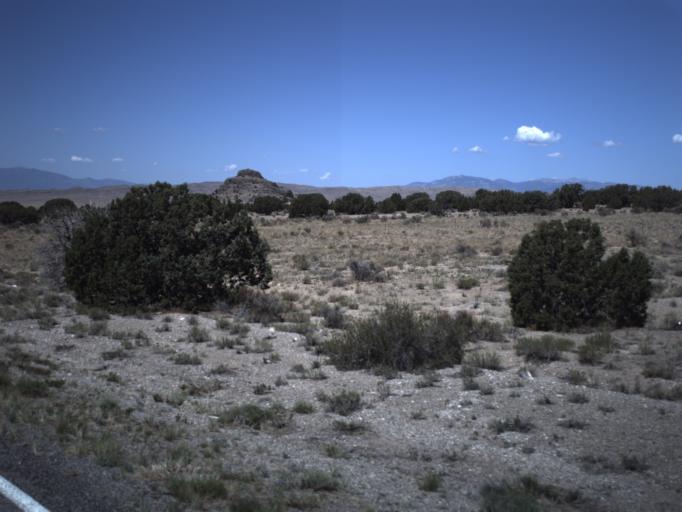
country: US
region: Utah
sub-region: Beaver County
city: Milford
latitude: 39.0777
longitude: -113.7075
